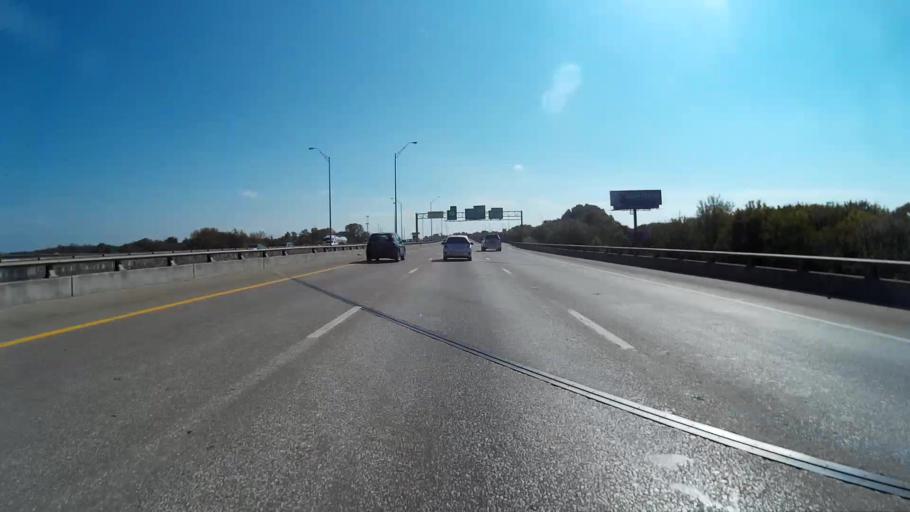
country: US
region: Texas
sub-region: Dallas County
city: Dallas
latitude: 32.7285
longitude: -96.7636
